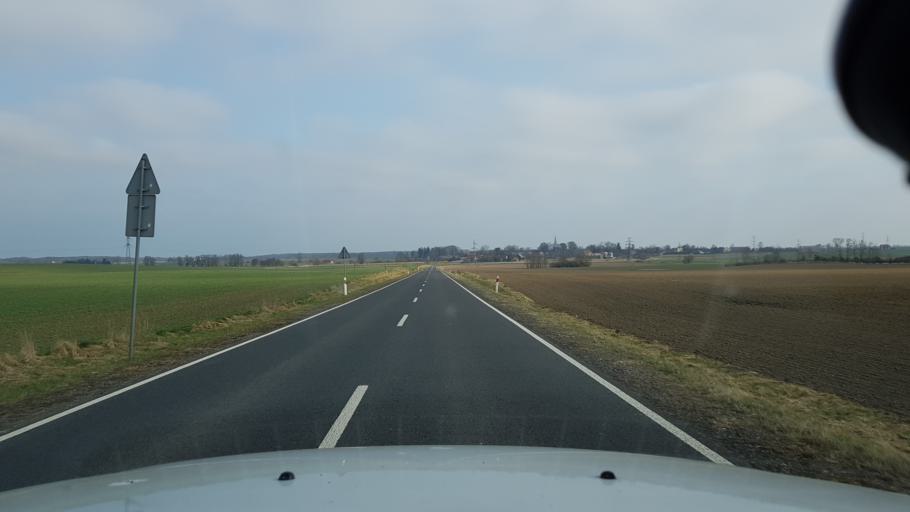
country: PL
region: West Pomeranian Voivodeship
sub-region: Powiat koszalinski
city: Sianow
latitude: 54.2838
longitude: 16.2708
